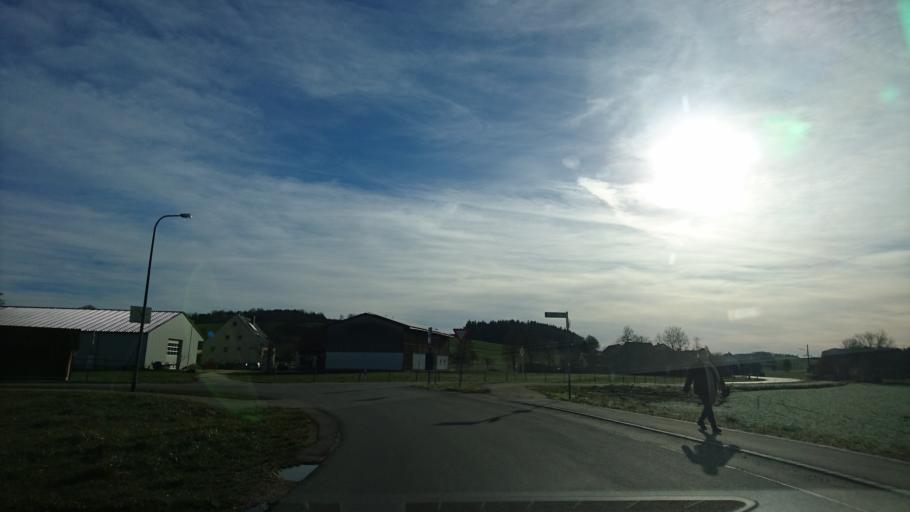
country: DE
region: Bavaria
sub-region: Swabia
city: Laugna
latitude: 48.5291
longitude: 10.7004
